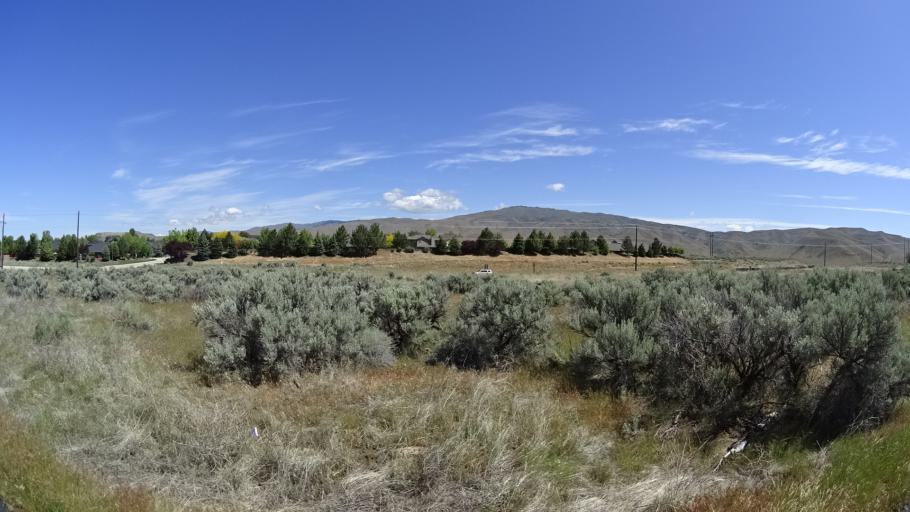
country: US
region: Idaho
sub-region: Ada County
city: Boise
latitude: 43.5424
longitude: -116.1138
